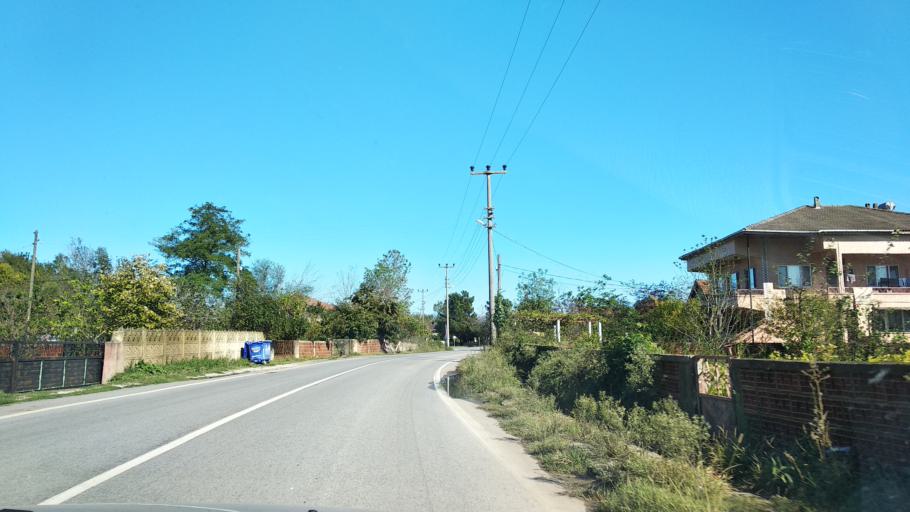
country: TR
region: Sakarya
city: Karasu
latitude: 41.1183
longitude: 30.6384
